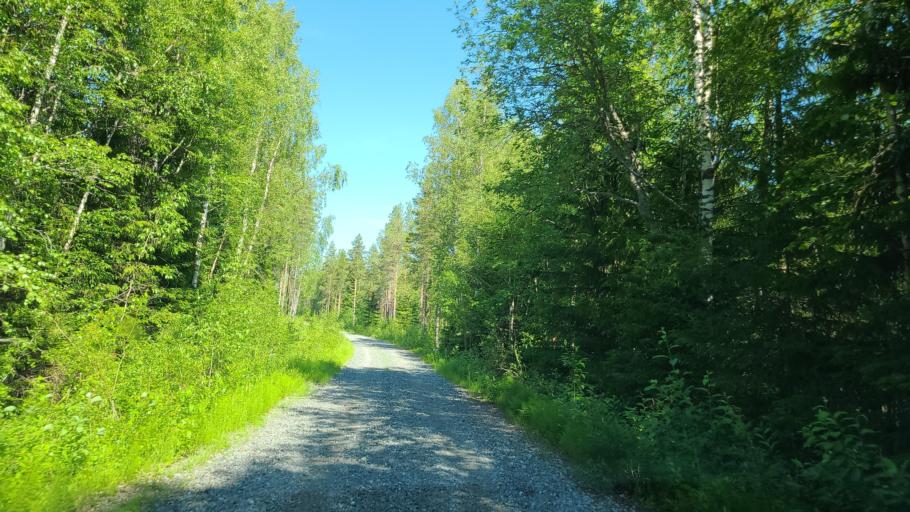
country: SE
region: Vaesterbotten
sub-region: Robertsfors Kommun
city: Robertsfors
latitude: 64.0941
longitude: 20.8351
